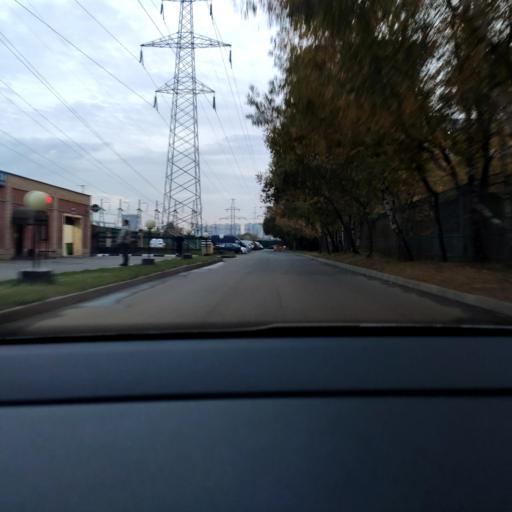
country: RU
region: Moscow
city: Bibirevo
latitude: 55.8841
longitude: 37.6105
